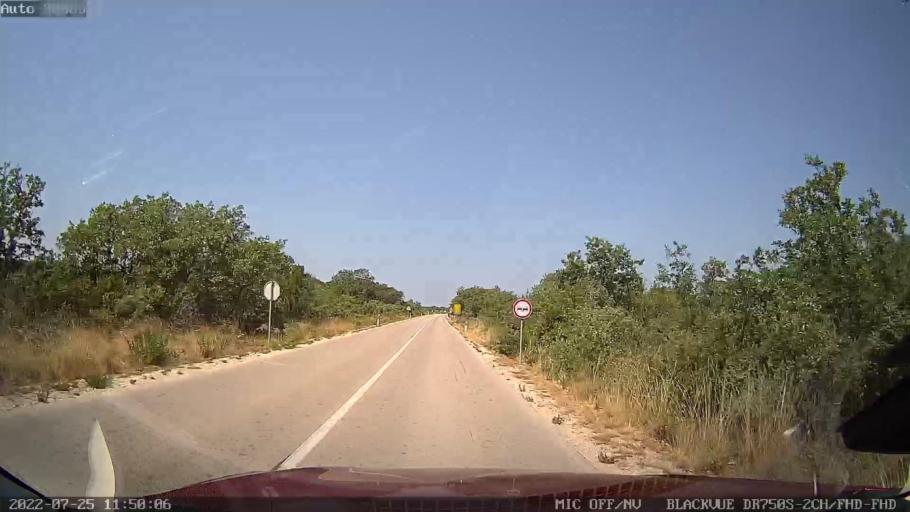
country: HR
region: Zadarska
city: Vrsi
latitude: 44.2359
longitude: 15.2704
